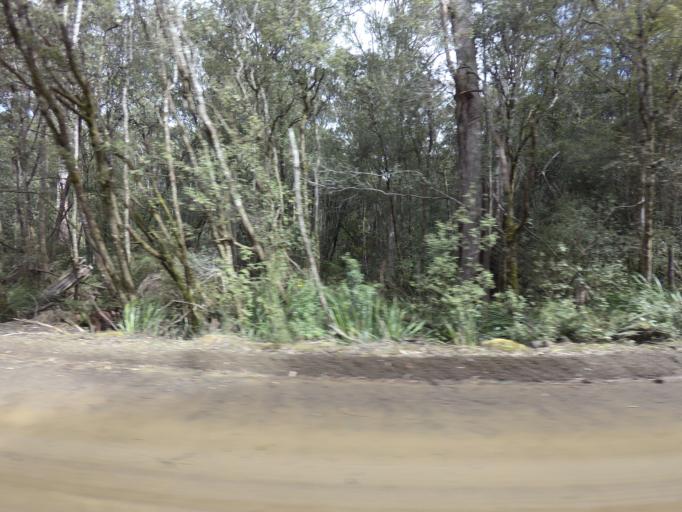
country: AU
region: Tasmania
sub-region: Huon Valley
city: Geeveston
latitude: -43.4096
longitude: 146.8721
